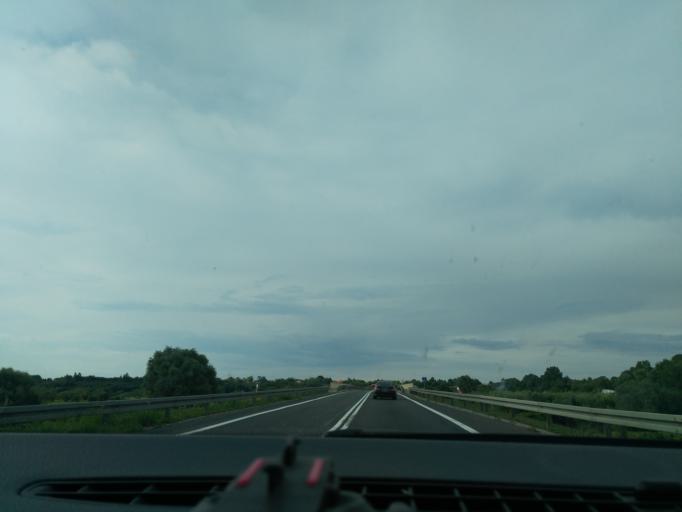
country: PL
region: Subcarpathian Voivodeship
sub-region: Powiat nizanski
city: Zarzecze
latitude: 50.5187
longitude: 22.1868
